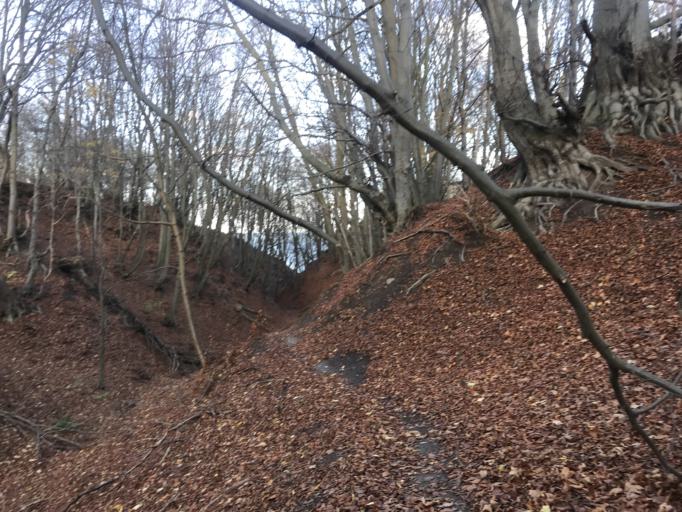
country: PL
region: Pomeranian Voivodeship
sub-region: Powiat pucki
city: Jastrzebia Gora
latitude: 54.8326
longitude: 18.3273
